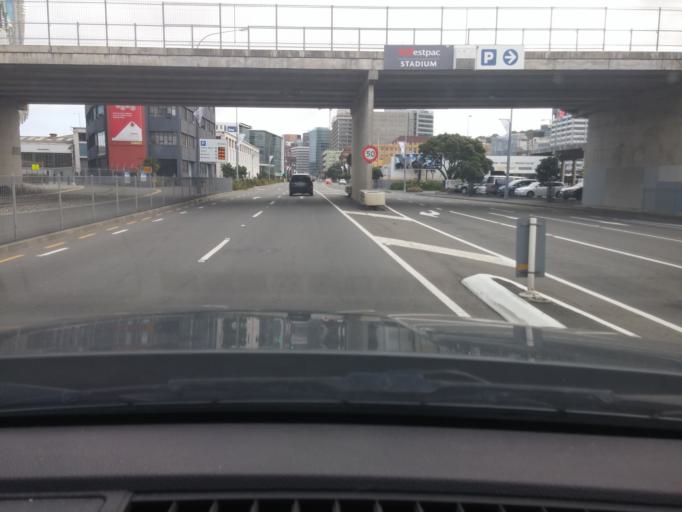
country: NZ
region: Wellington
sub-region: Wellington City
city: Wellington
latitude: -41.2768
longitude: 174.7838
